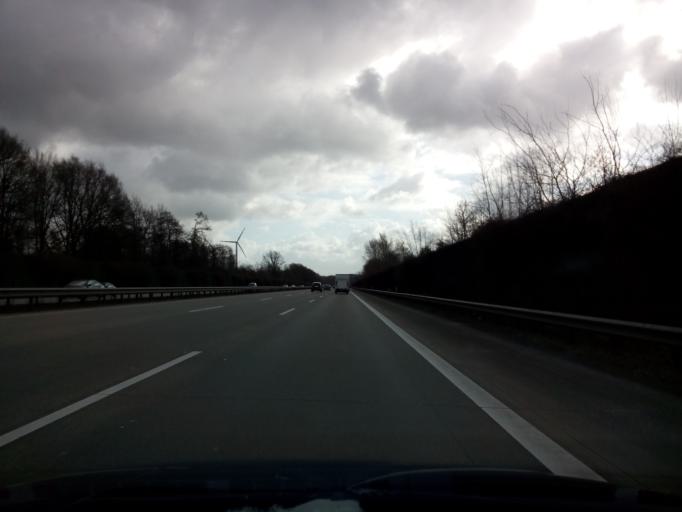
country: DE
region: Bremen
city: Bremen
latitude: 53.1258
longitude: 8.7742
